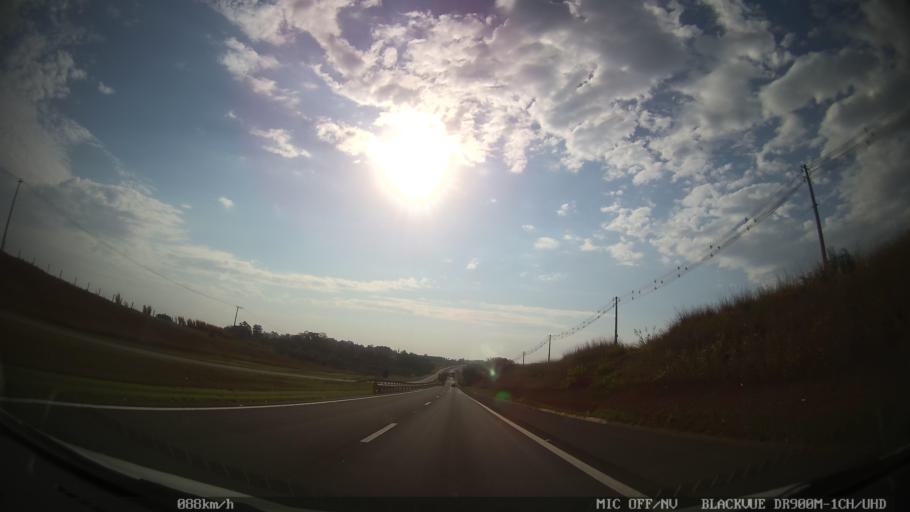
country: BR
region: Sao Paulo
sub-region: Paulinia
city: Paulinia
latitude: -22.6982
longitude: -47.1492
